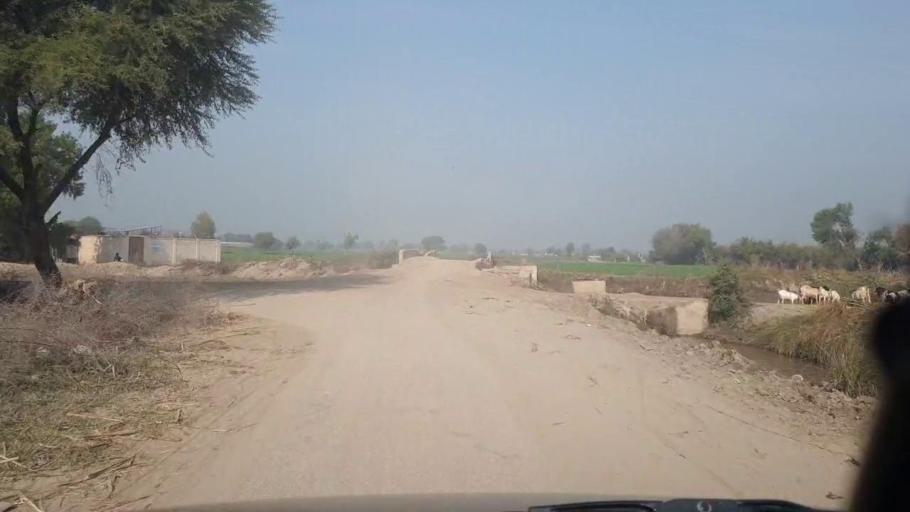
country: PK
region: Sindh
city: Shahdadpur
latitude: 26.0346
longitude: 68.5393
